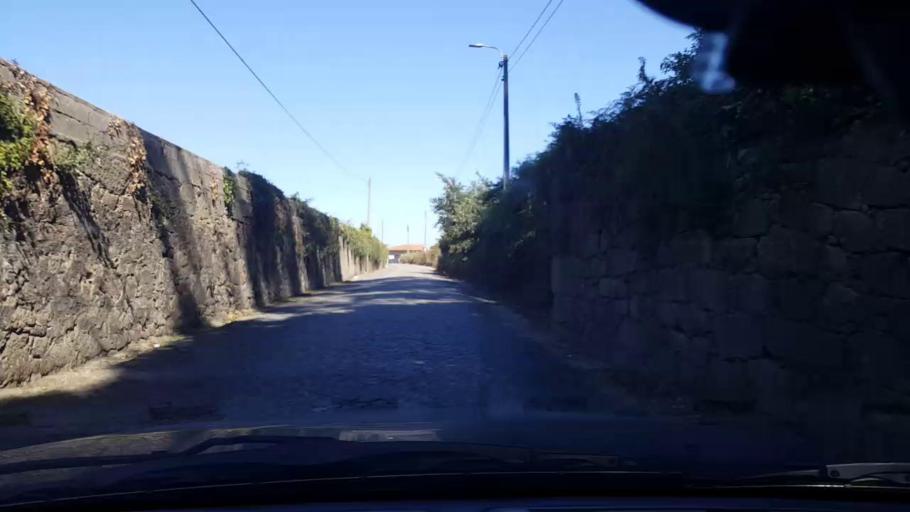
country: PT
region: Porto
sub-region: Maia
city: Gemunde
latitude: 41.2840
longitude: -8.6726
